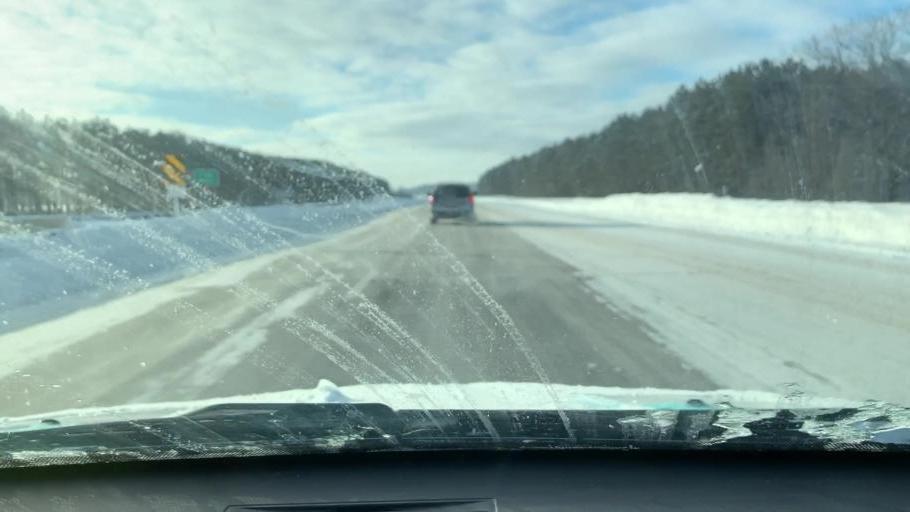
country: US
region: Michigan
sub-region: Wexford County
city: Cadillac
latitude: 44.2793
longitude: -85.3887
